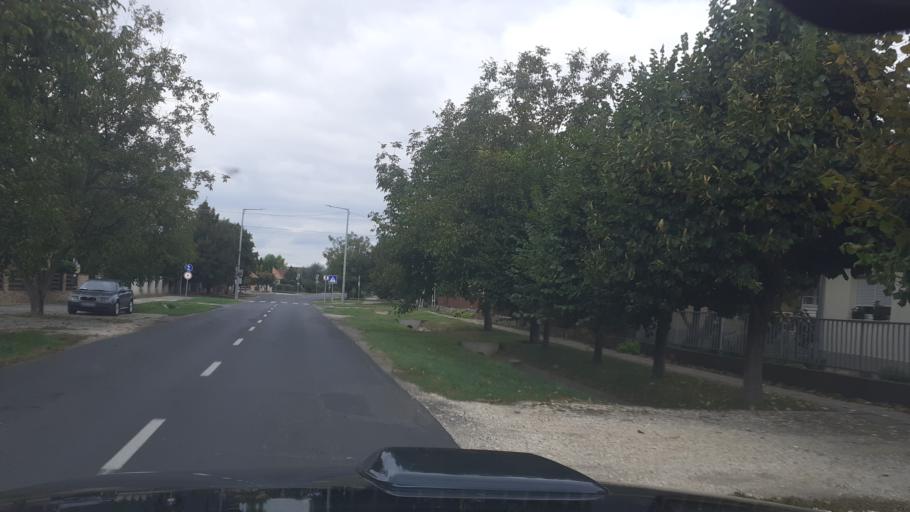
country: HU
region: Fejer
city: Racalmas
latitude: 47.0293
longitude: 18.9373
